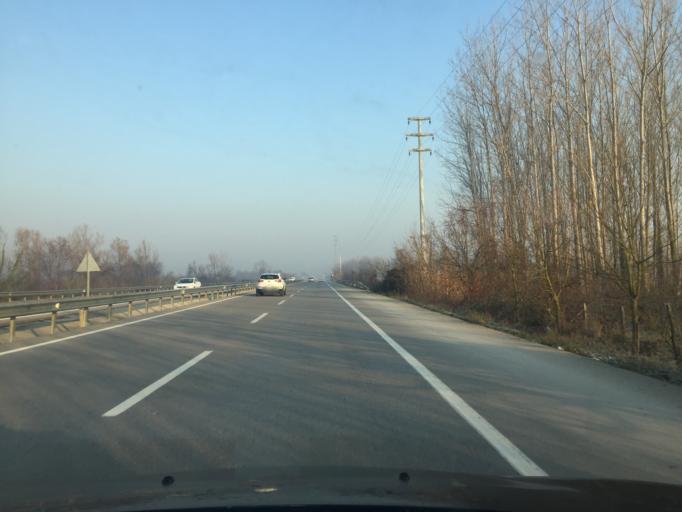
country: TR
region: Sakarya
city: Akyazi
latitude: 40.6825
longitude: 30.5769
